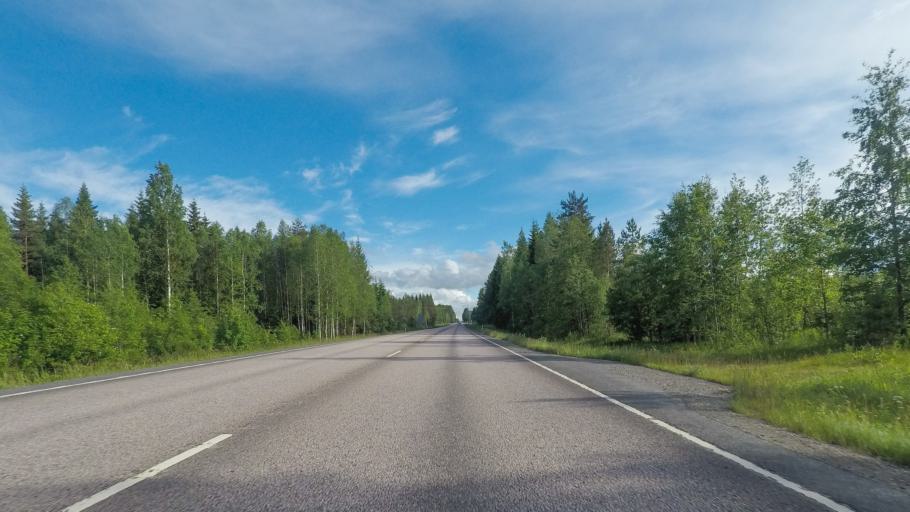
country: FI
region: Central Finland
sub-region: Joutsa
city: Leivonmaeki
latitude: 61.9048
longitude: 26.1164
